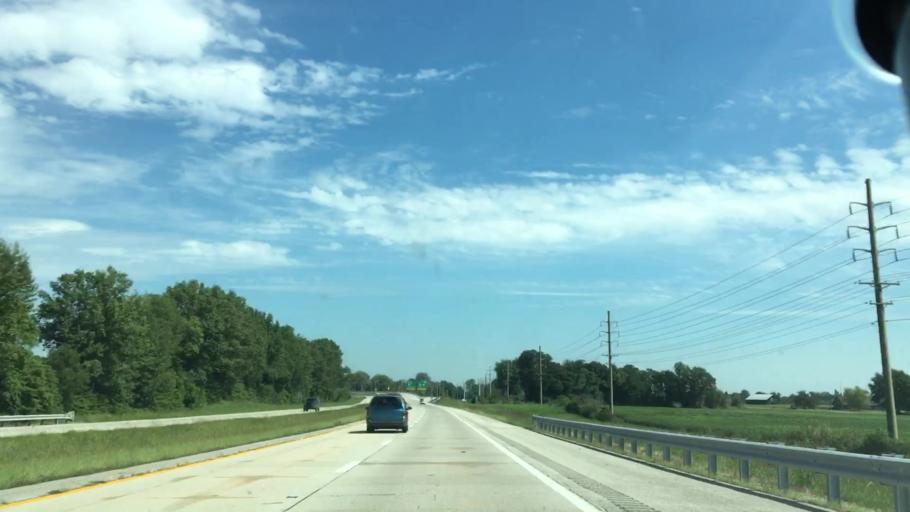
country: US
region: Kentucky
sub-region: Daviess County
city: Owensboro
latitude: 37.7656
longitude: -87.1734
